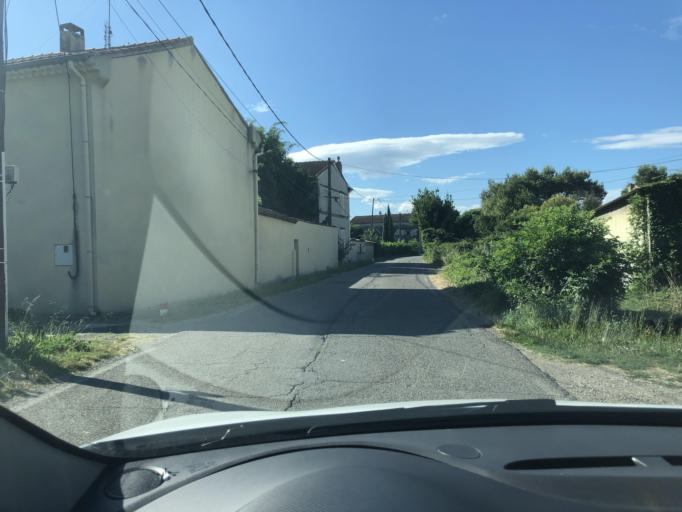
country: FR
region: Provence-Alpes-Cote d'Azur
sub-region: Departement des Bouches-du-Rhone
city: Chateaurenard
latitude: 43.8924
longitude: 4.8456
